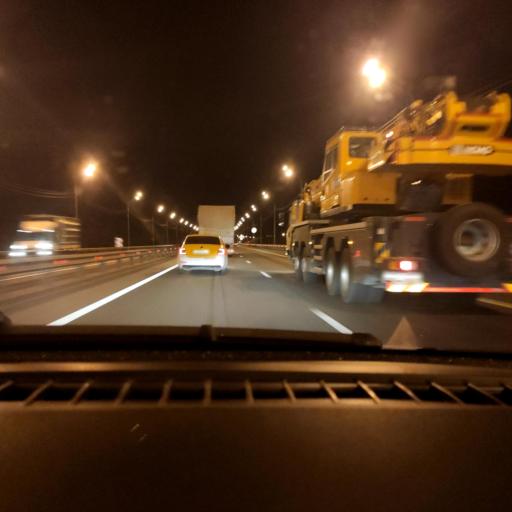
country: RU
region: Lipetsk
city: Khlevnoye
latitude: 52.2350
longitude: 39.0813
